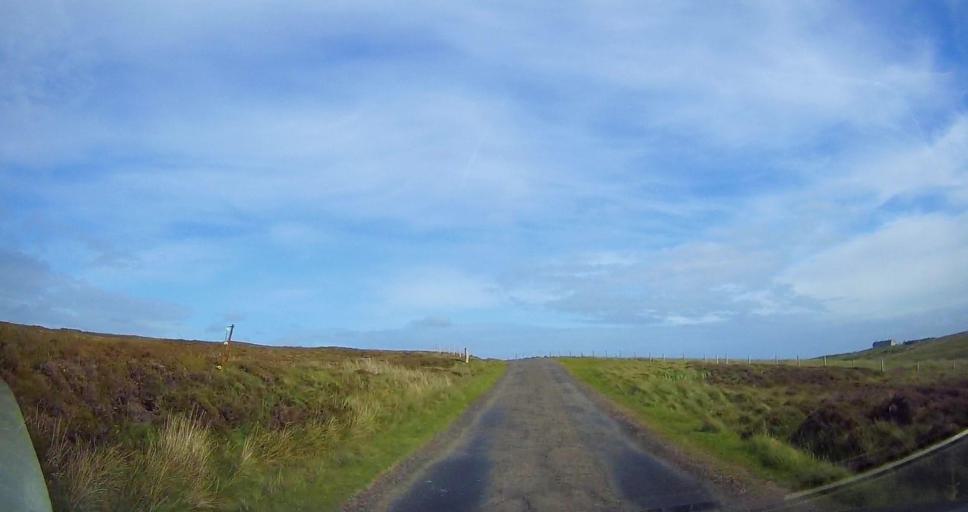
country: GB
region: Scotland
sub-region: Orkney Islands
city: Stromness
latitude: 58.8537
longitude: -3.2084
